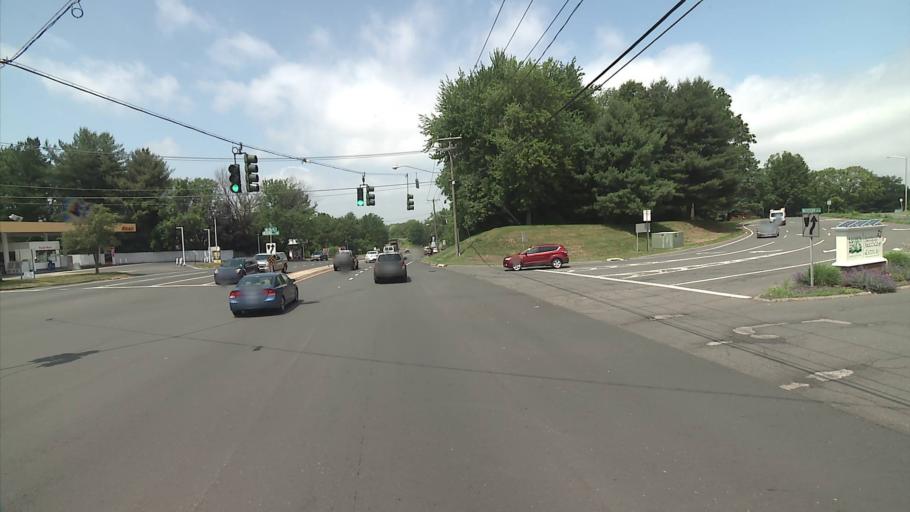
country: US
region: Connecticut
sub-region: Hartford County
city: Glastonbury Center
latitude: 41.7143
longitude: -72.5907
